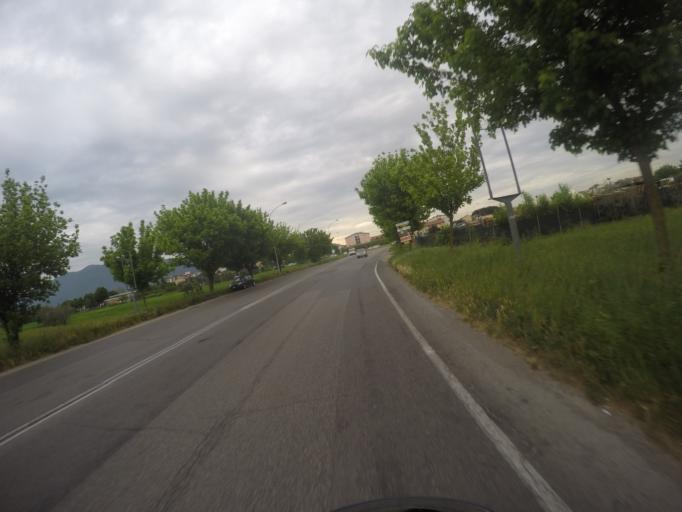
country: IT
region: Tuscany
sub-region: Provincia di Prato
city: Prato
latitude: 43.8946
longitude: 11.0741
